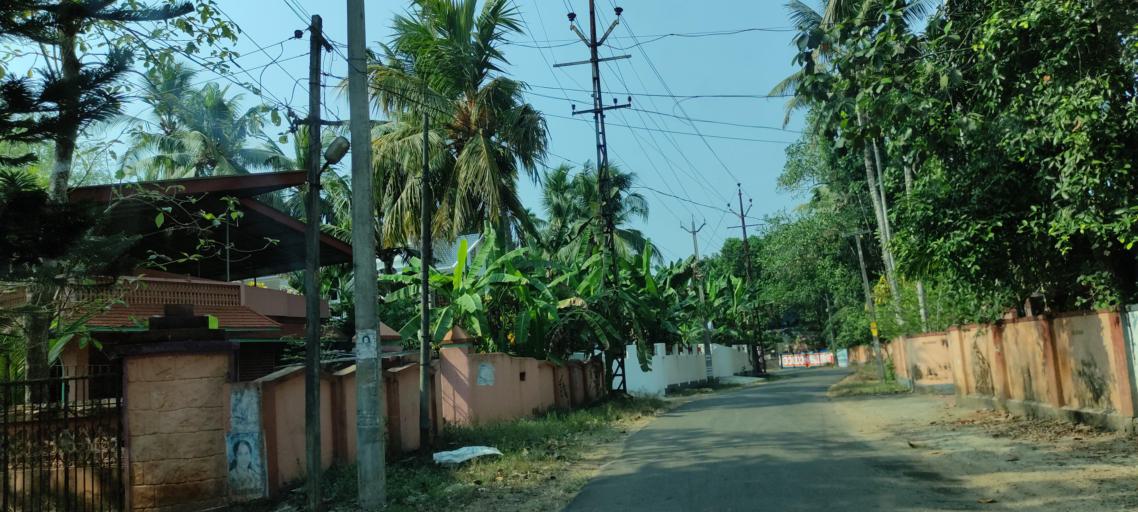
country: IN
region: Kerala
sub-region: Pattanamtitta
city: Tiruvalla
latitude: 9.3581
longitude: 76.5152
